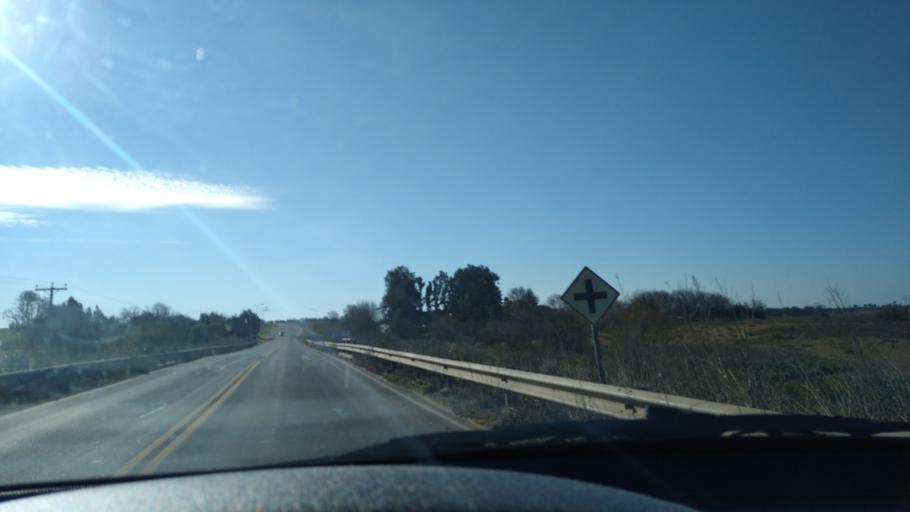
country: AR
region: Entre Rios
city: Aranguren
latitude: -32.4053
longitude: -60.3242
